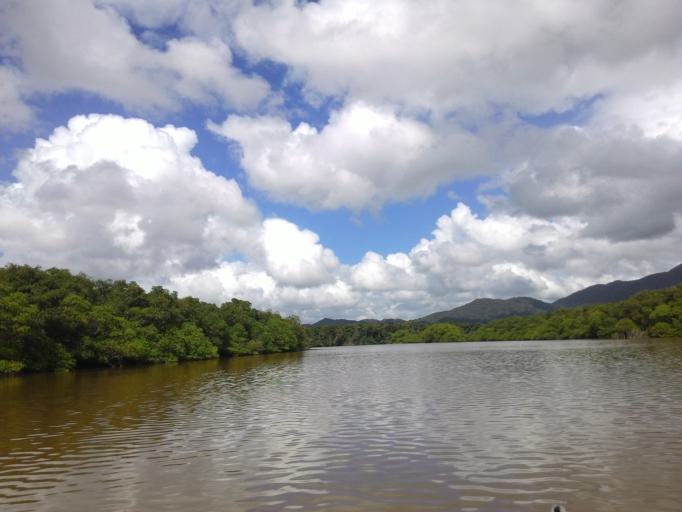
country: BR
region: Sao Paulo
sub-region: Cananeia
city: Cananeia
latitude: -24.8829
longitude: -47.8023
